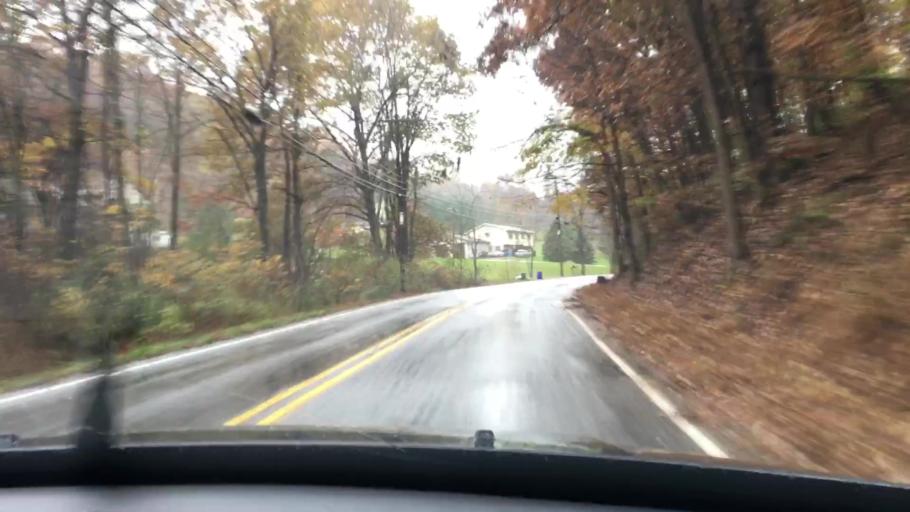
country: US
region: Pennsylvania
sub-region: York County
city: Glen Rock
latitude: 39.7712
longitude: -76.7532
